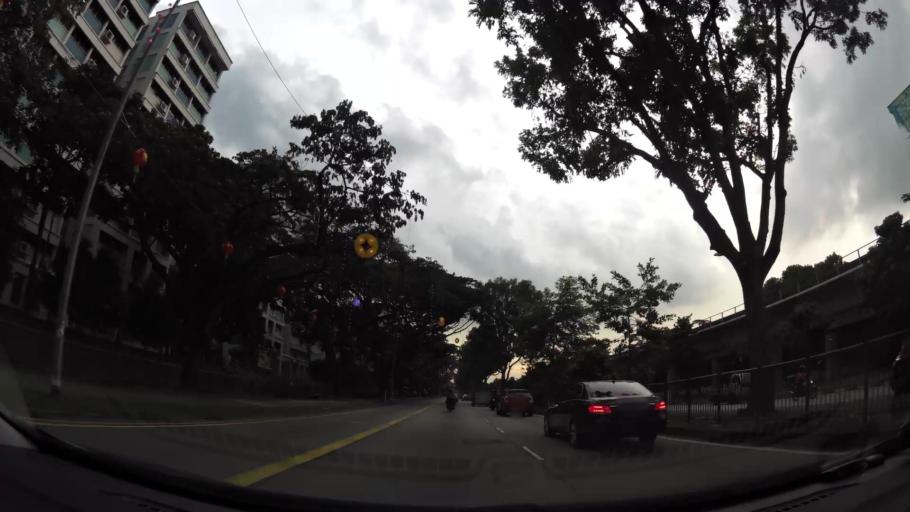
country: MY
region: Johor
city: Kampung Pasir Gudang Baru
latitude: 1.4158
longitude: 103.8326
